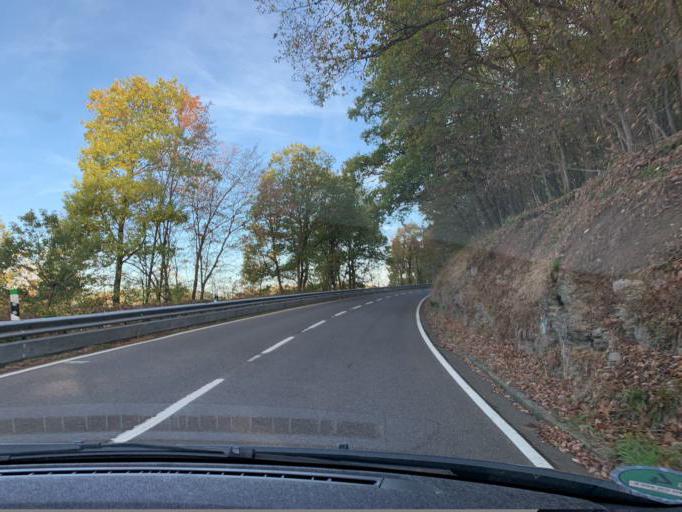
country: DE
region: North Rhine-Westphalia
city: Heimbach
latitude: 50.6251
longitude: 6.4723
